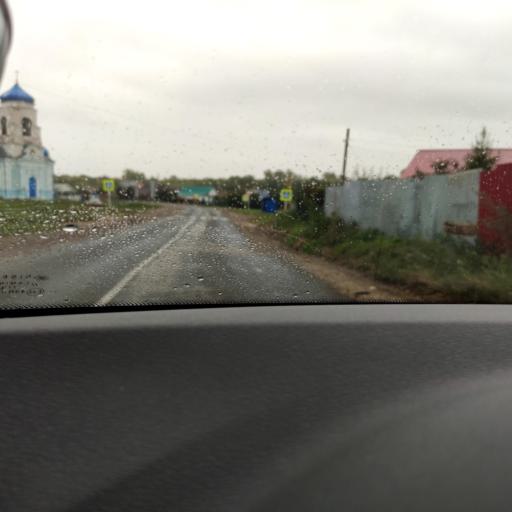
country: RU
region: Samara
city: Yelkhovka
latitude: 53.7441
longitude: 50.2604
